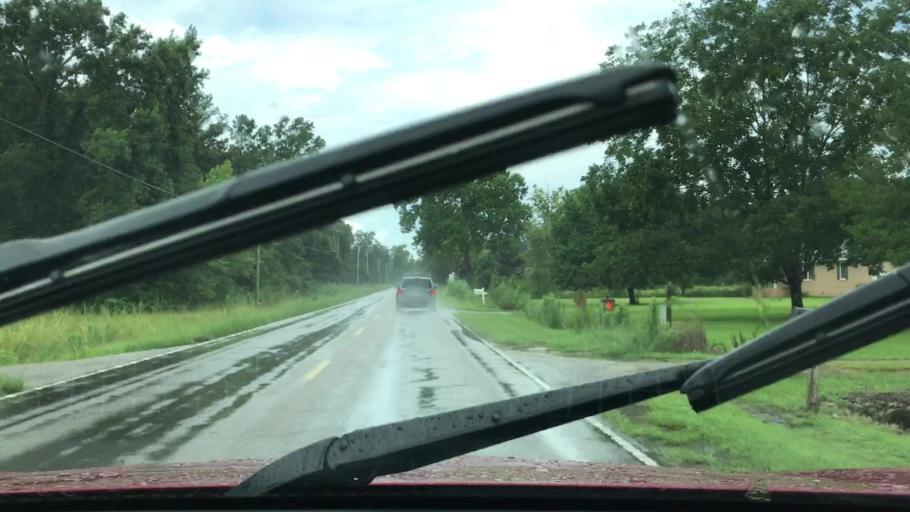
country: US
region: South Carolina
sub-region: Horry County
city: Red Hill
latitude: 33.8607
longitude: -78.9960
